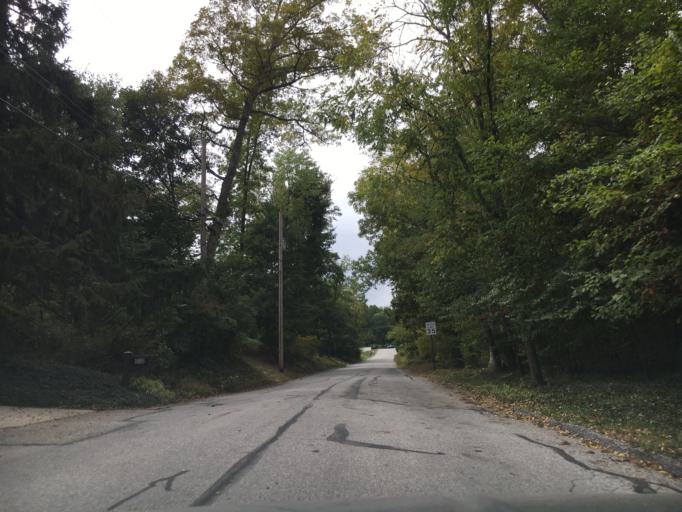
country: US
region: Pennsylvania
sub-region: York County
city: Grantley
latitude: 39.9340
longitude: -76.7233
